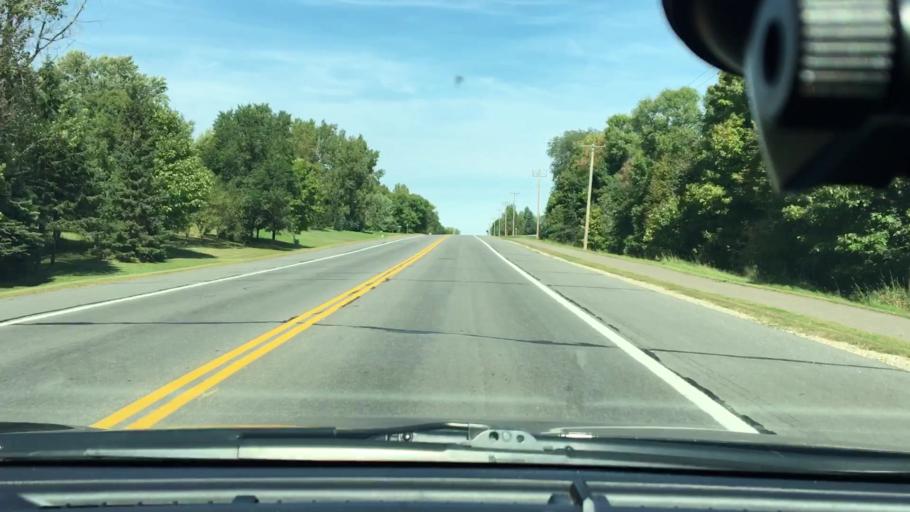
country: US
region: Minnesota
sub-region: Wright County
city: Hanover
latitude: 45.1639
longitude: -93.6659
